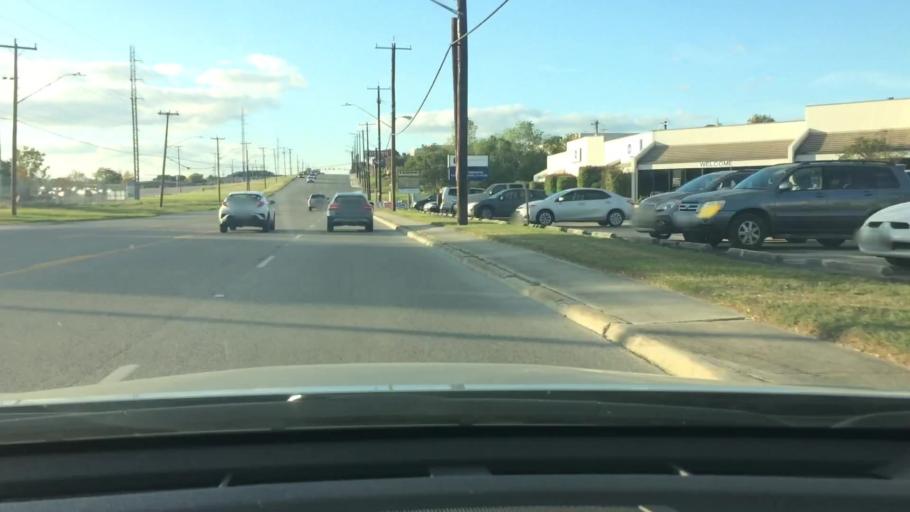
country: US
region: Texas
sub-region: Bexar County
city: Hollywood Park
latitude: 29.5494
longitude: -98.4634
